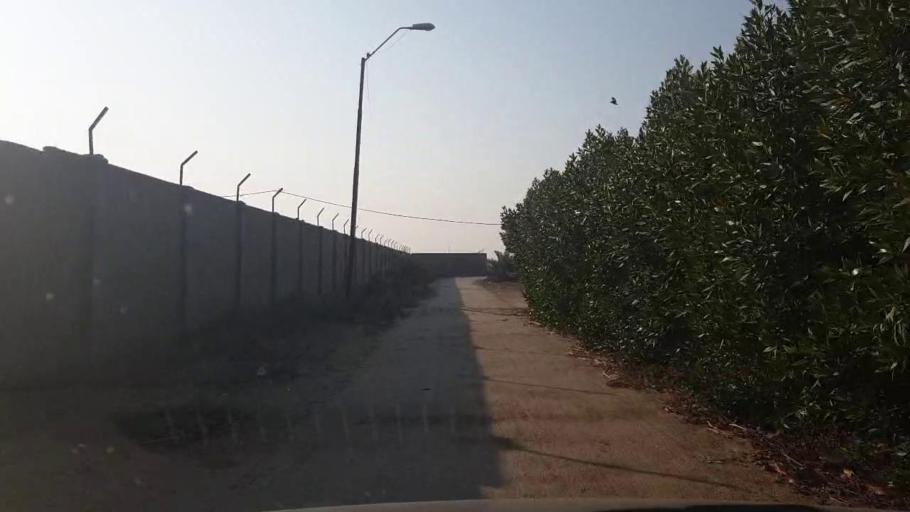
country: PK
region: Sindh
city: Tando Adam
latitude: 25.7484
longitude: 68.6402
